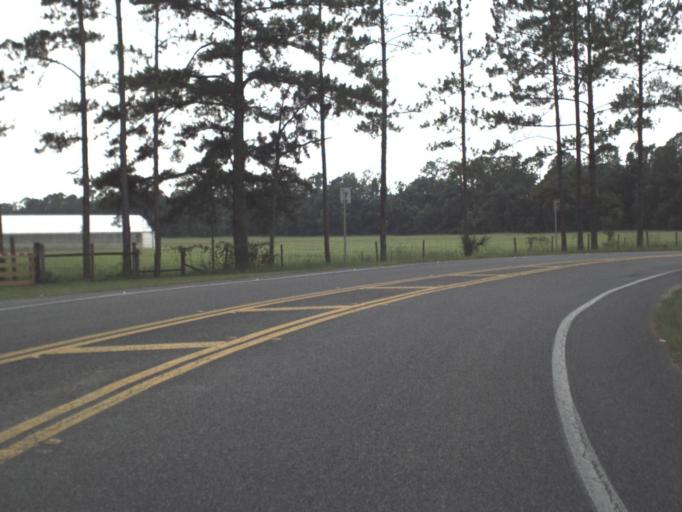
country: US
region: Florida
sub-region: Levy County
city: Chiefland
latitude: 29.4751
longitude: -82.8453
